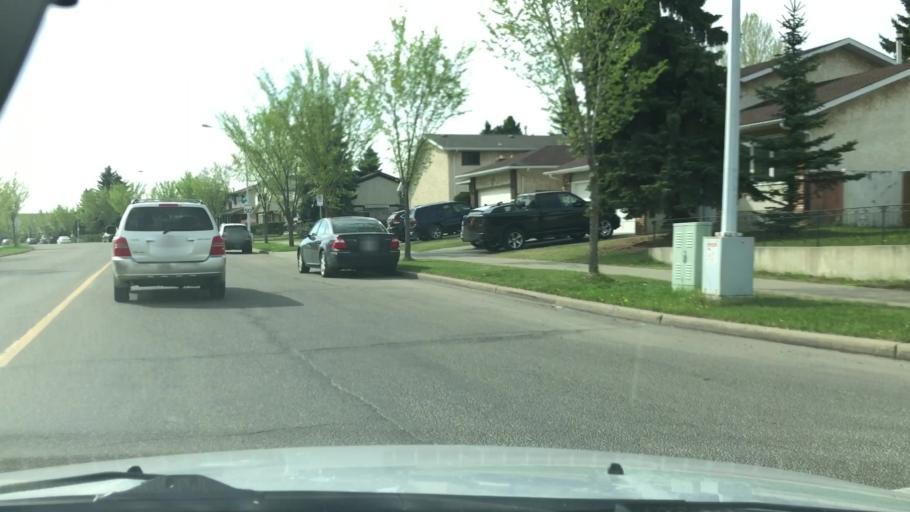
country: CA
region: Alberta
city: Edmonton
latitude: 53.6038
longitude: -113.5303
